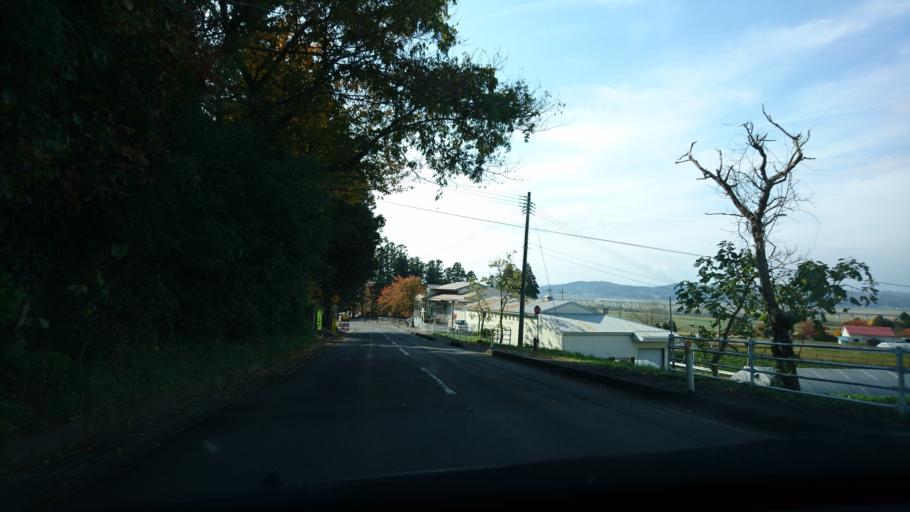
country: JP
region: Iwate
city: Ichinoseki
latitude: 38.9657
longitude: 141.1732
